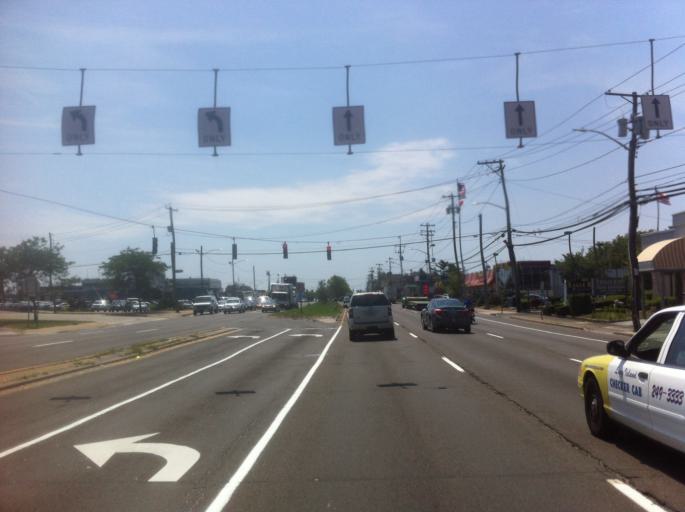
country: US
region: New York
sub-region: Nassau County
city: Hicksville
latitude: 40.7797
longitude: -73.5311
